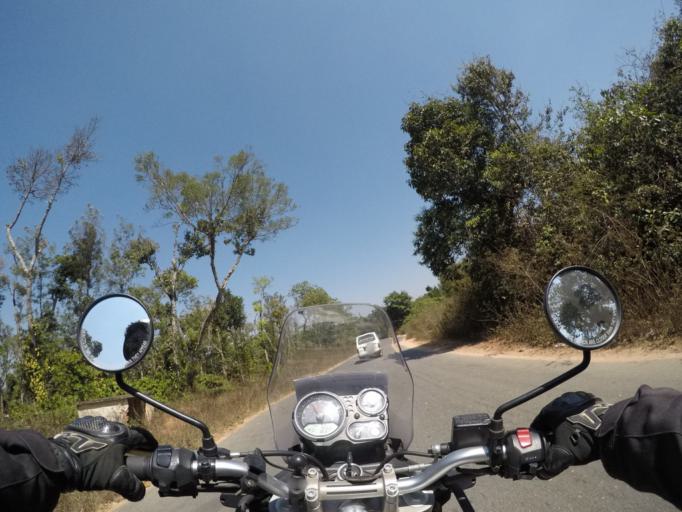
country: IN
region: Karnataka
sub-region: Chikmagalur
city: Mudigere
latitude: 13.0677
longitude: 75.6786
